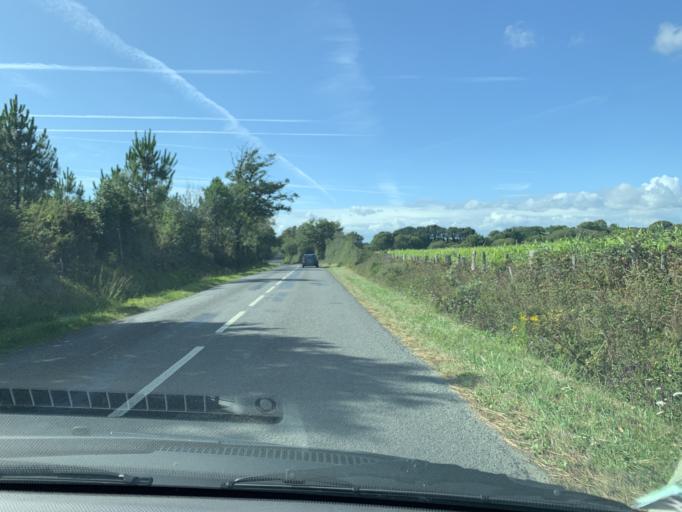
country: FR
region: Pays de la Loire
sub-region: Departement de la Loire-Atlantique
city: Asserac
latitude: 47.4441
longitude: -2.4067
